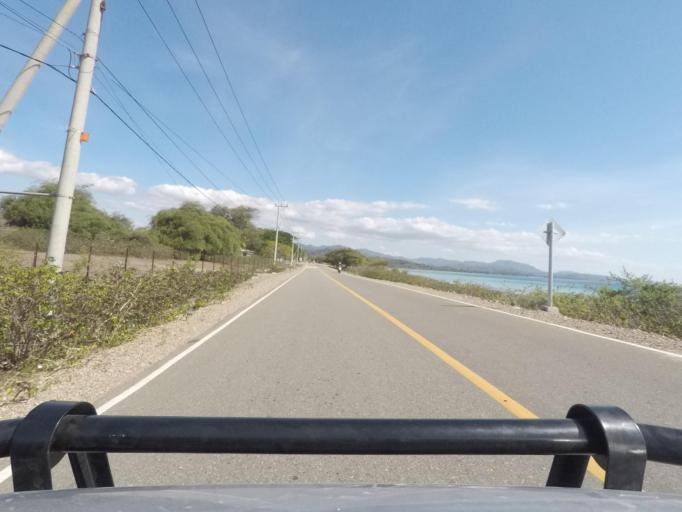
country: ID
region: East Nusa Tenggara
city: Atambua
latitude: -8.9310
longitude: 124.9811
